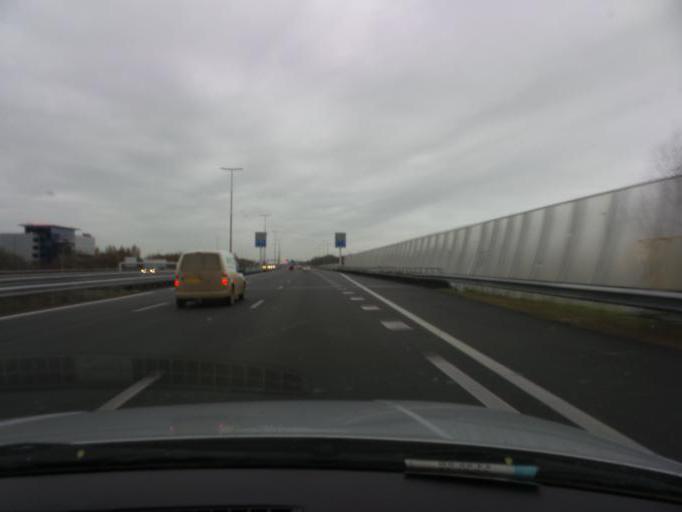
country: NL
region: Overijssel
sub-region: Gemeente Zwolle
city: Zwolle
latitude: 52.5070
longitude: 6.0680
